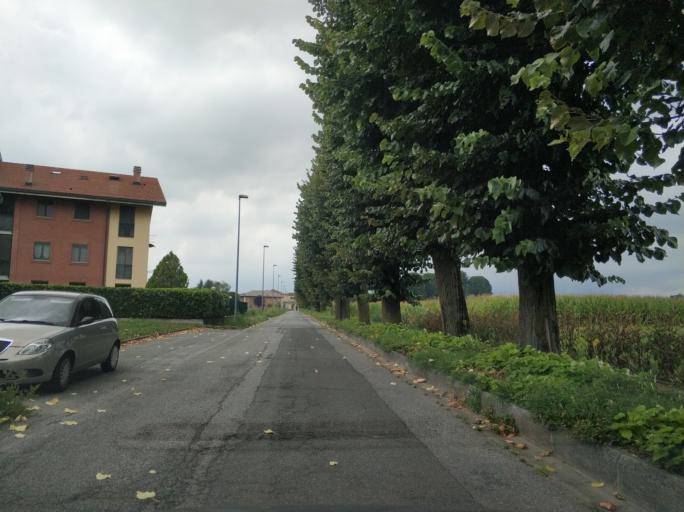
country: IT
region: Piedmont
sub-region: Provincia di Torino
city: Caselle Torinese
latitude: 45.1782
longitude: 7.6320
